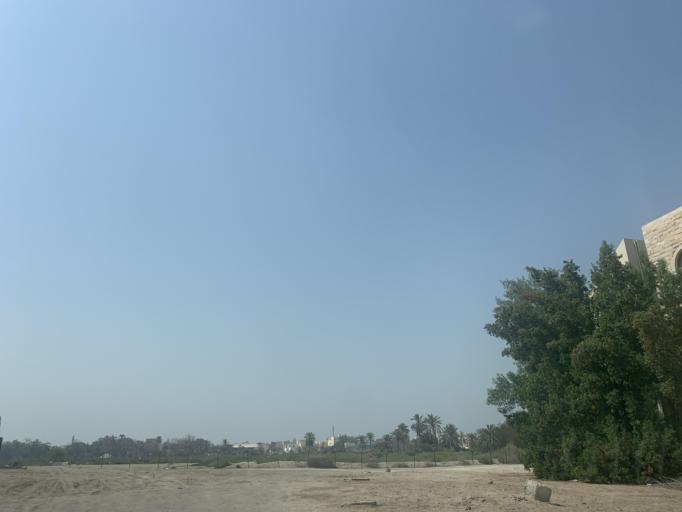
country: BH
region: Manama
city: Jidd Hafs
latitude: 26.2096
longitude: 50.4992
